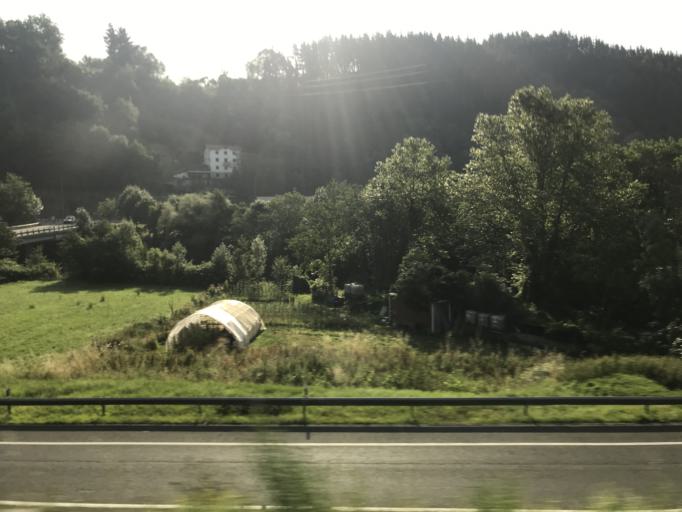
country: ES
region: Basque Country
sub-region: Provincia de Guipuzcoa
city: Arama
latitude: 43.0590
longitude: -2.1709
